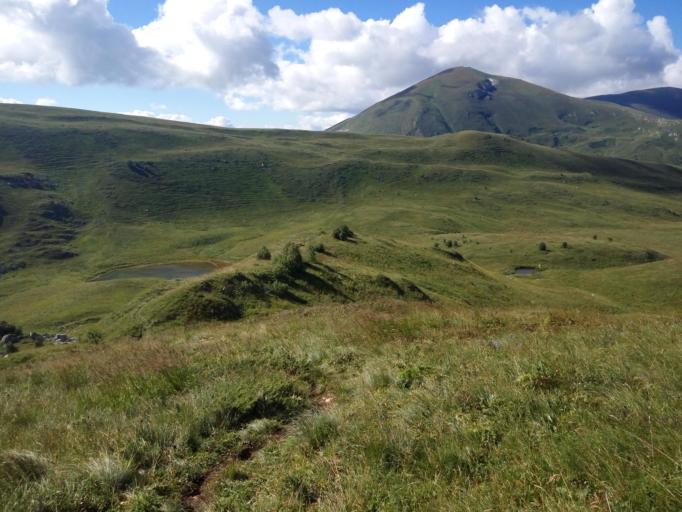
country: RU
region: Adygeya
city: Kamennomostskiy
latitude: 44.0077
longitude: 39.9049
